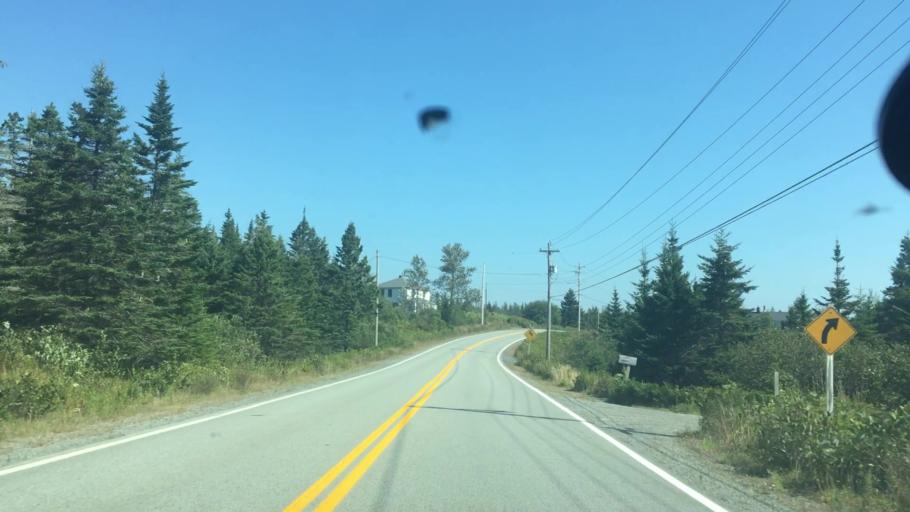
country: CA
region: Nova Scotia
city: New Glasgow
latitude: 44.9297
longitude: -62.2965
